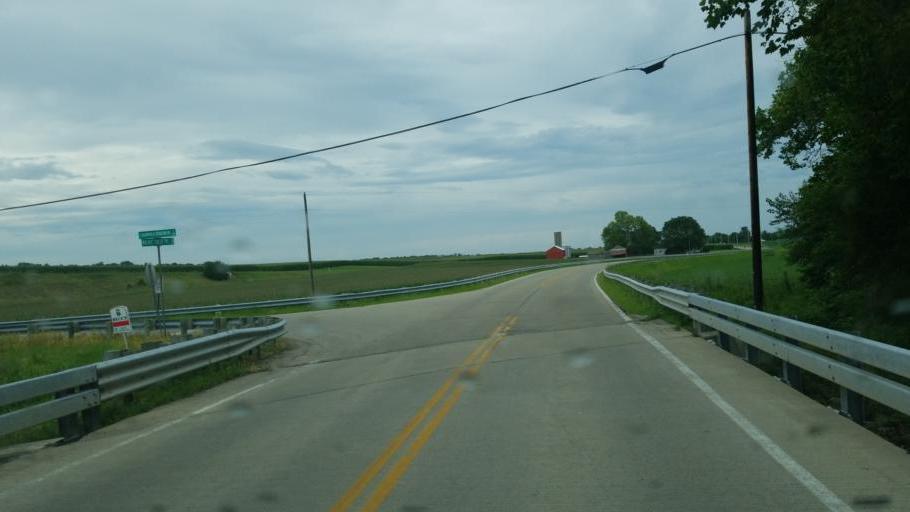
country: US
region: Ohio
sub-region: Pickaway County
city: Ashville
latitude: 39.7050
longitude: -82.9216
